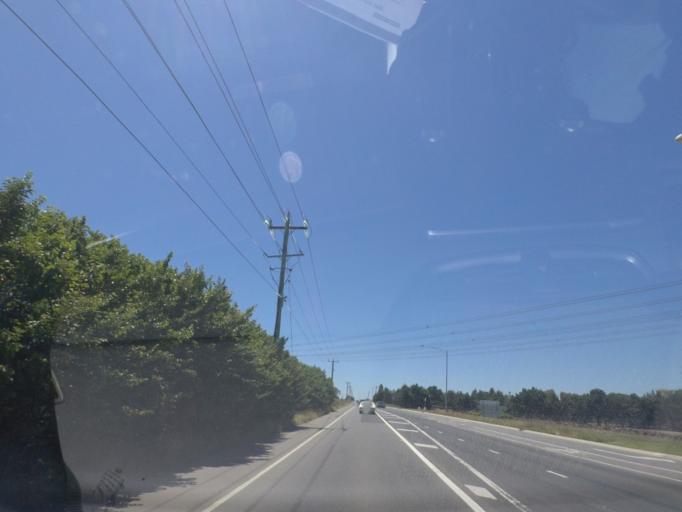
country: AU
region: Victoria
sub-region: Whittlesea
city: Epping
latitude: -37.6221
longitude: 145.0289
